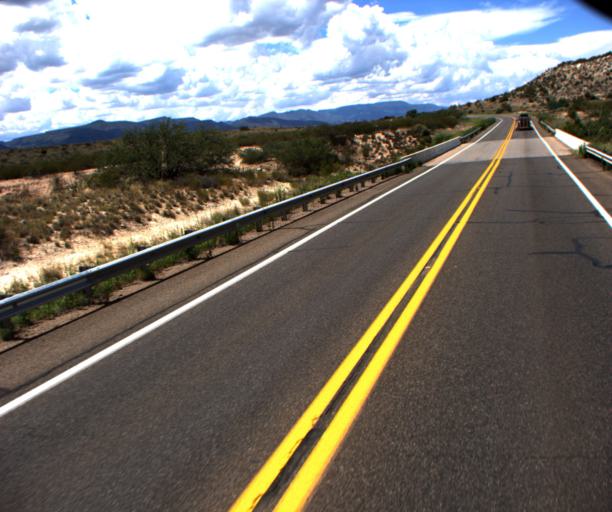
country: US
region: Arizona
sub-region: Yavapai County
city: Camp Verde
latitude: 34.5320
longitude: -111.8105
